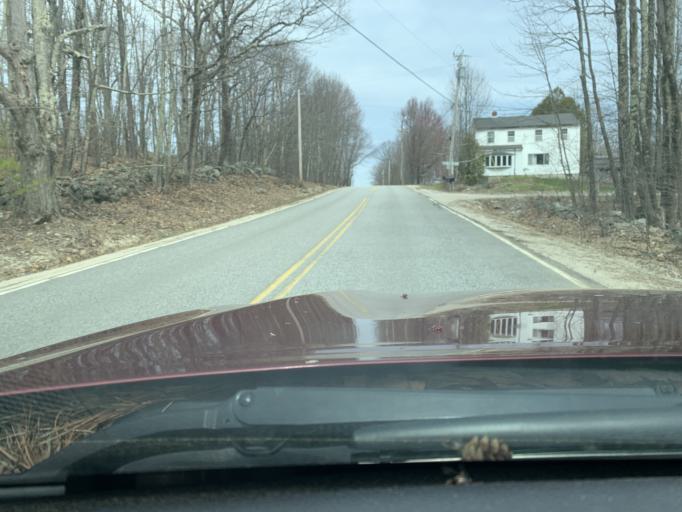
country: US
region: Maine
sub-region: Cumberland County
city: Raymond
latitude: 43.9551
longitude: -70.3870
